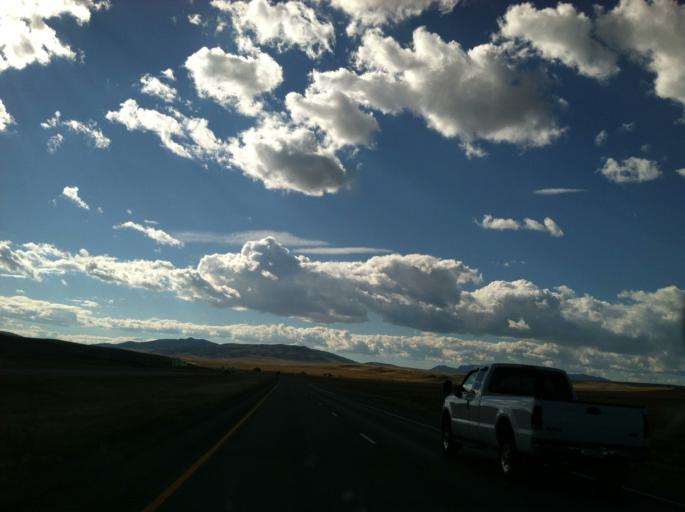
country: US
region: Montana
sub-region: Gallatin County
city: Three Forks
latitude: 45.9149
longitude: -111.7432
